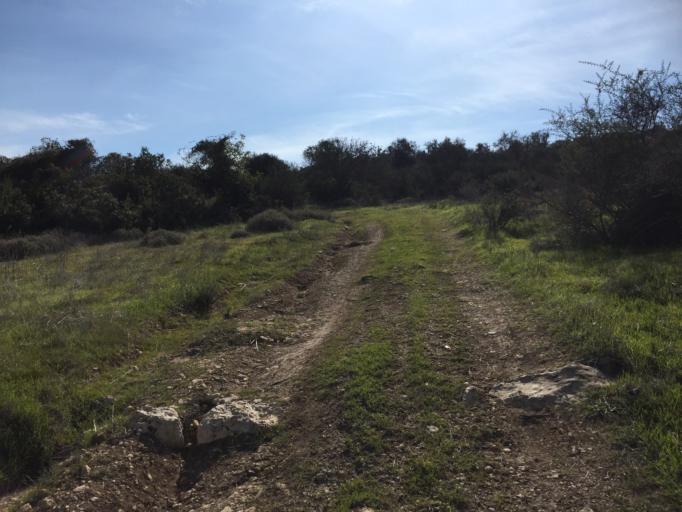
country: CY
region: Limassol
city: Mouttagiaka
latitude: 34.7462
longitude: 33.1133
